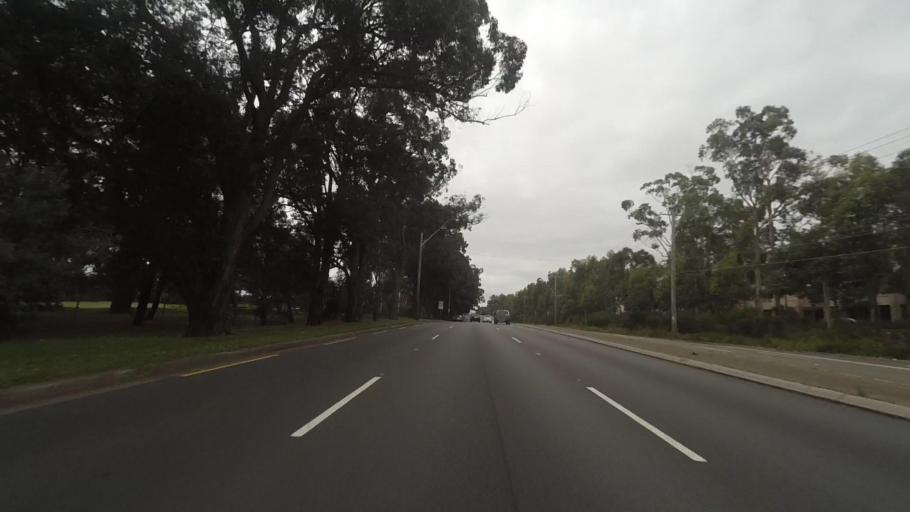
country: AU
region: New South Wales
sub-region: Auburn
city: Berala
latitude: -33.8816
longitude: 151.0405
